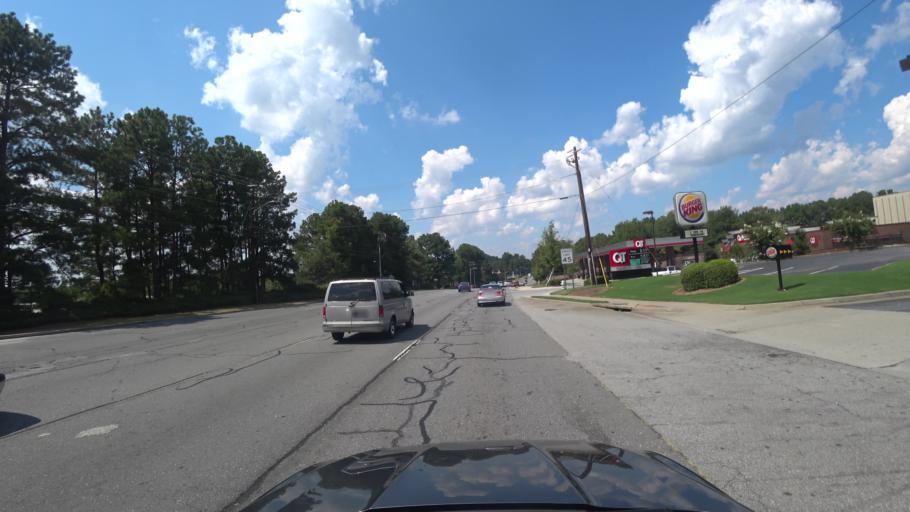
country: US
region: Georgia
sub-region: Gwinnett County
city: Norcross
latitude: 33.9409
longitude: -84.2494
